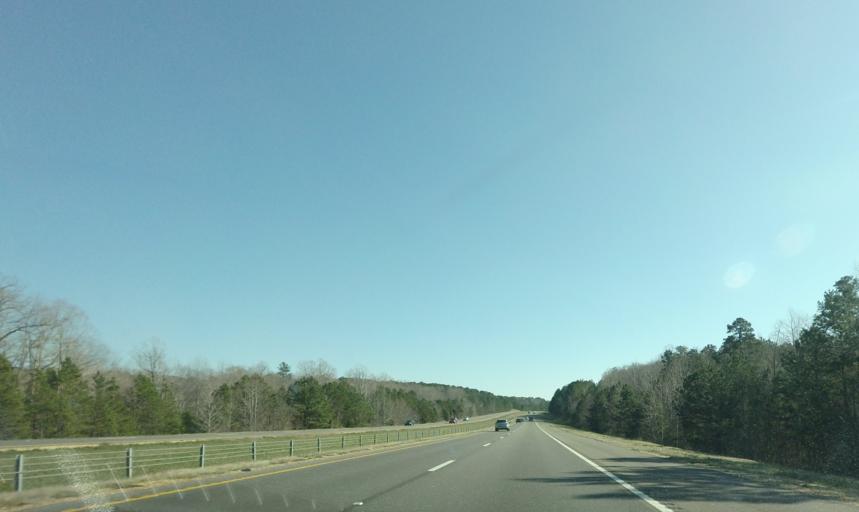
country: US
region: Mississippi
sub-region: Union County
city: New Albany
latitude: 34.5959
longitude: -89.1807
